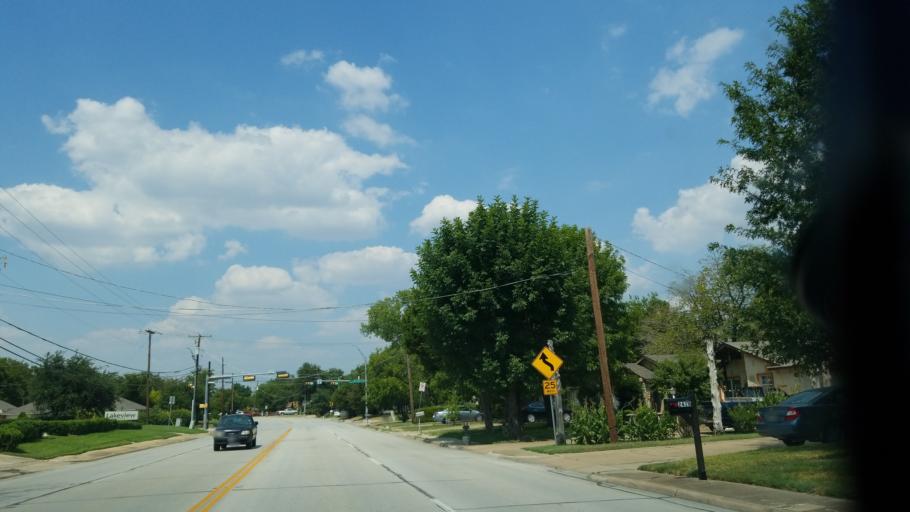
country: US
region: Texas
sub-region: Dallas County
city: Grand Prairie
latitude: 32.7096
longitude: -96.9856
